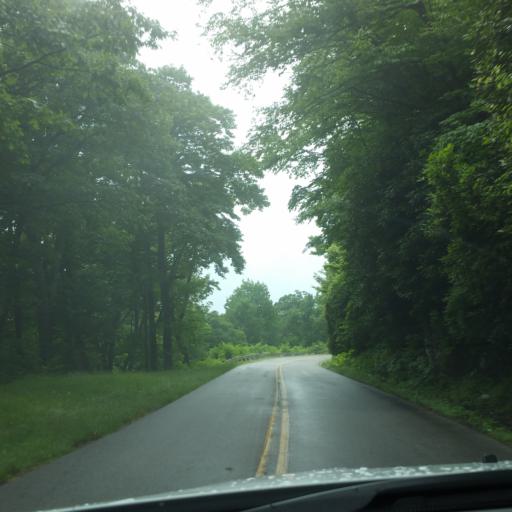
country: US
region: North Carolina
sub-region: Transylvania County
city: Brevard
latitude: 35.3545
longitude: -82.7999
